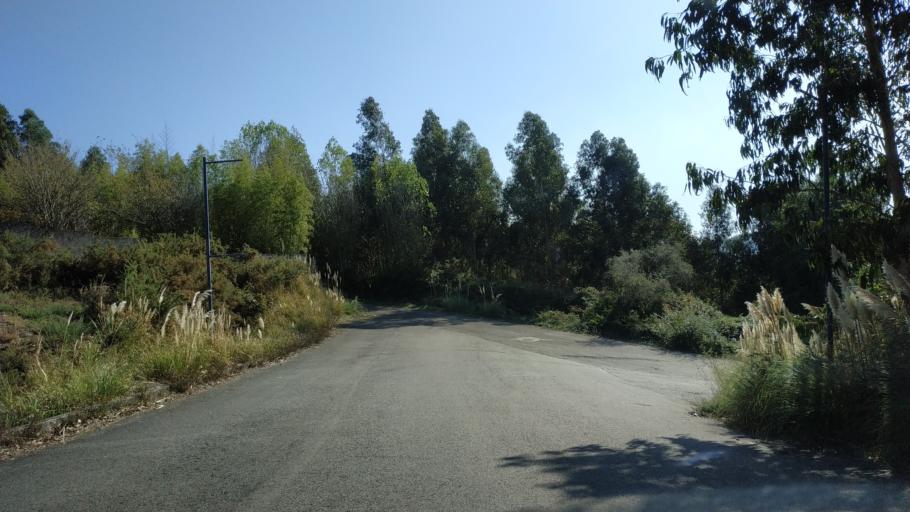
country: ES
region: Galicia
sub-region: Provincia da Coruna
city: Culleredo
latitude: 43.3226
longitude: -8.3915
